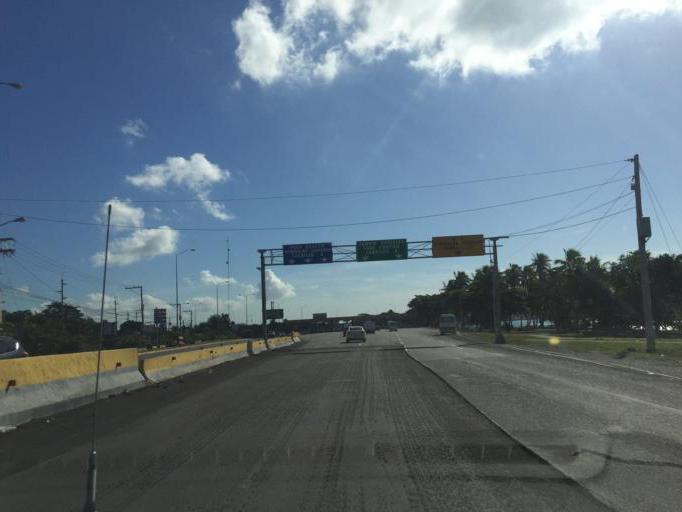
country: DO
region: Santo Domingo
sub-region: Santo Domingo
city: Boca Chica
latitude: 18.4537
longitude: -69.6939
